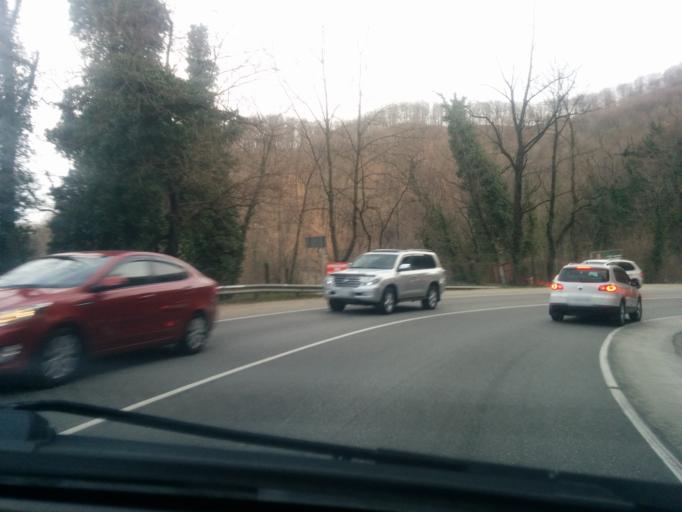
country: RU
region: Krasnodarskiy
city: Agoy
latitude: 44.1186
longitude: 39.0492
